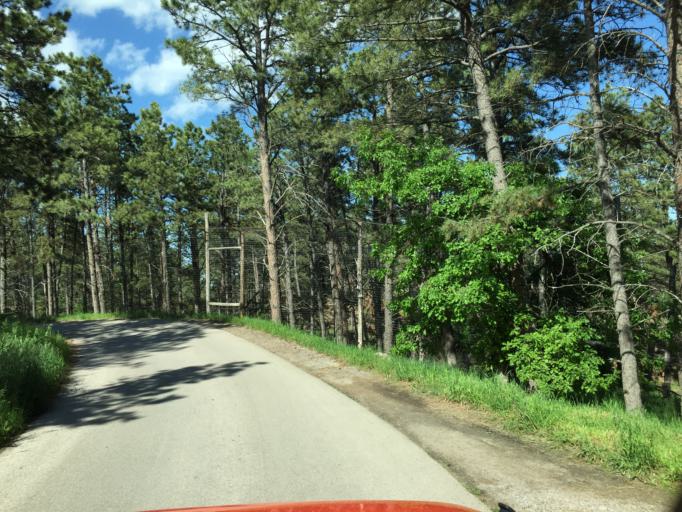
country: US
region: South Dakota
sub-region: Pennington County
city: Colonial Pine Hills
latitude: 43.9791
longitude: -103.2942
